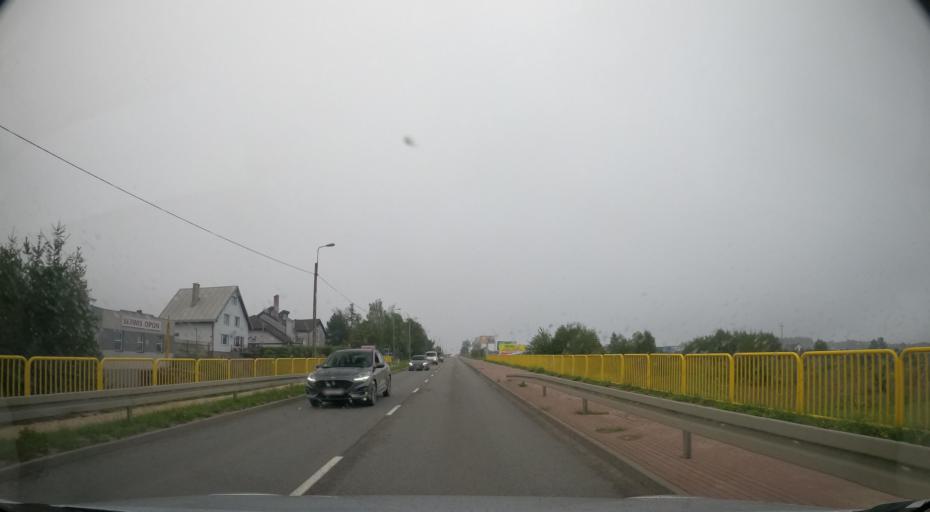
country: PL
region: Pomeranian Voivodeship
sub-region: Powiat kartuski
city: Chwaszczyno
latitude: 54.4432
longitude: 18.4042
